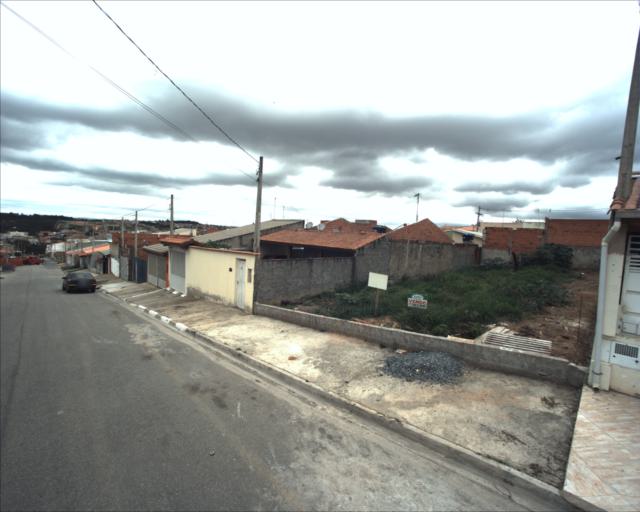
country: BR
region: Sao Paulo
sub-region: Sorocaba
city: Sorocaba
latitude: -23.4359
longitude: -47.5049
